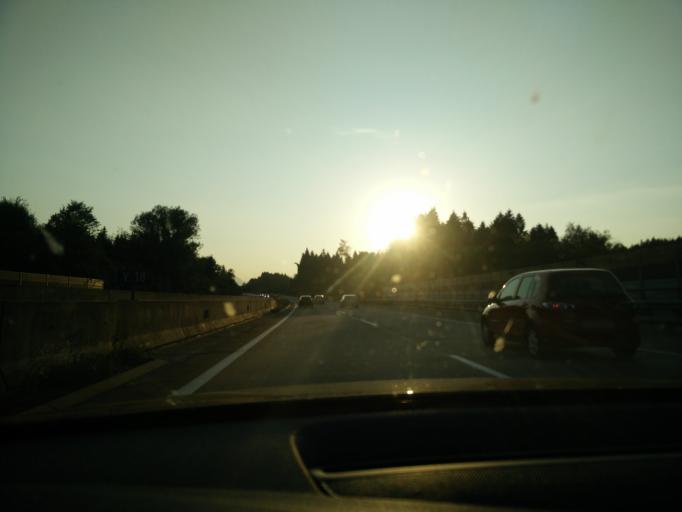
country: AT
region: Carinthia
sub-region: Politischer Bezirk Villach Land
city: Wernberg
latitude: 46.6242
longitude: 13.9649
